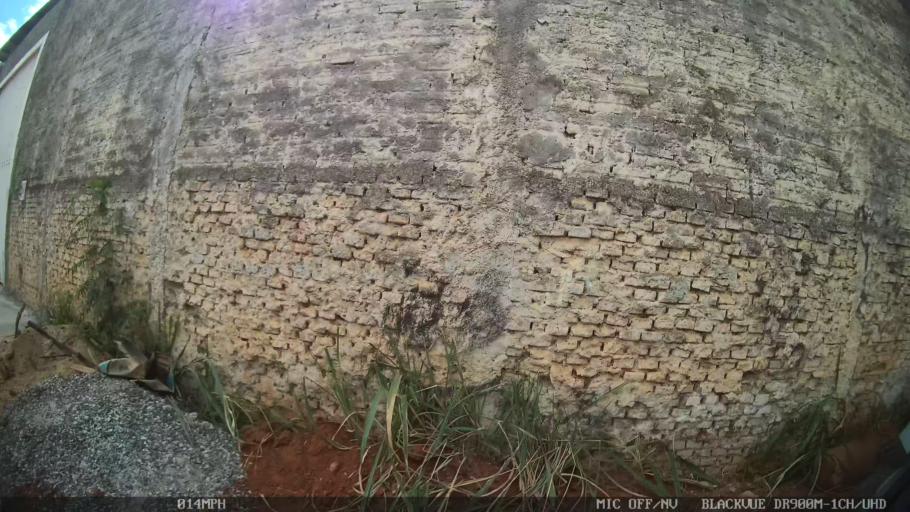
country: BR
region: Sao Paulo
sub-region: Bady Bassitt
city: Bady Bassitt
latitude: -20.8130
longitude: -49.5147
